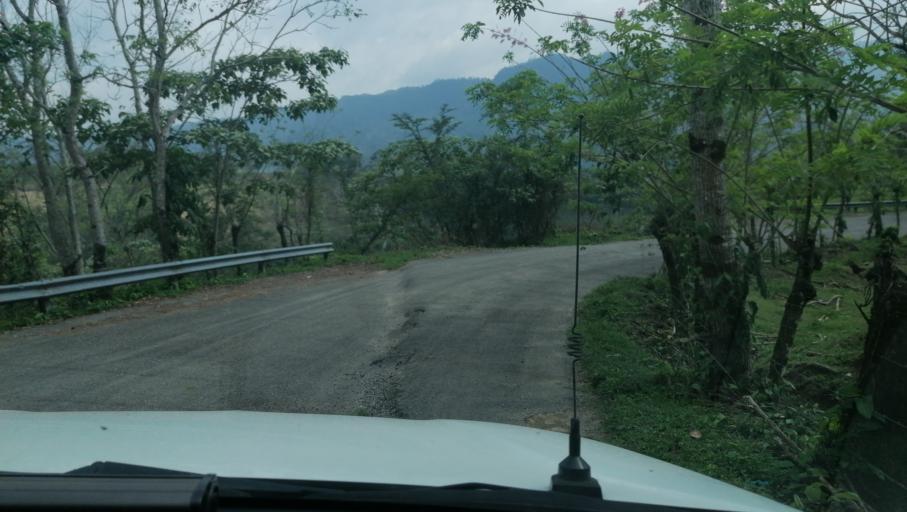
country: MX
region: Chiapas
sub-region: Francisco Leon
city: San Miguel la Sardina
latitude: 17.2290
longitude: -93.3417
